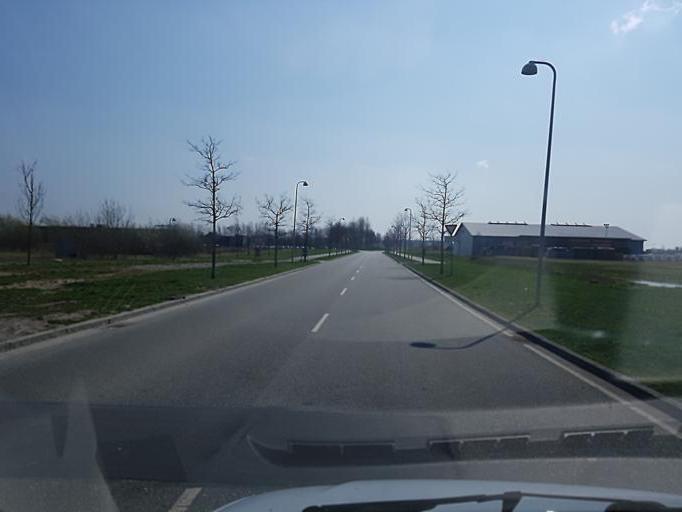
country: DK
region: South Denmark
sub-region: Odense Kommune
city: Neder Holluf
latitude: 55.3743
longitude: 10.4848
